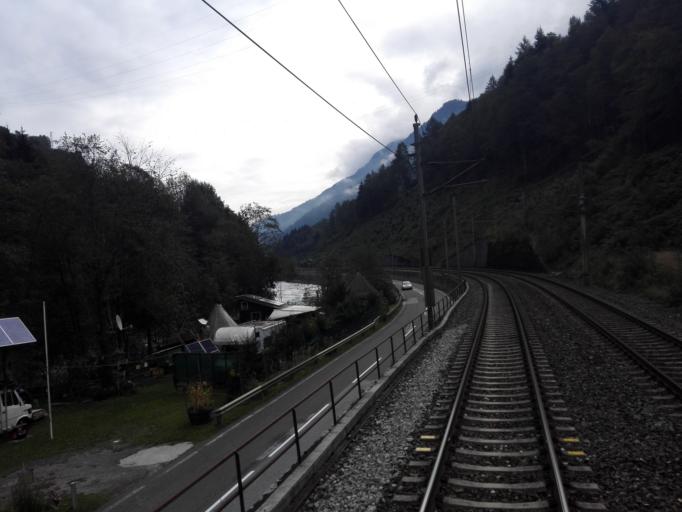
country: AT
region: Salzburg
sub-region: Politischer Bezirk Zell am See
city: Lend
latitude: 47.2986
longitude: 13.0757
